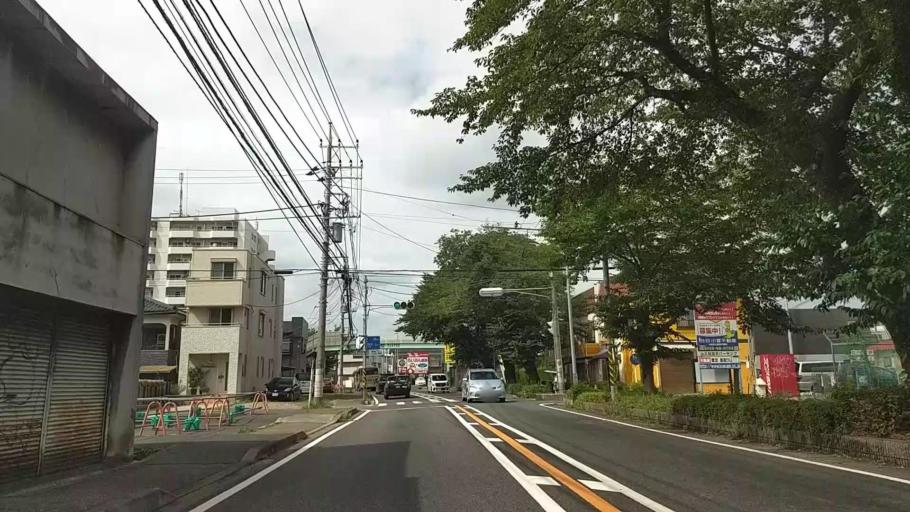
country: JP
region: Kanagawa
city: Minami-rinkan
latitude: 35.4501
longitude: 139.4677
